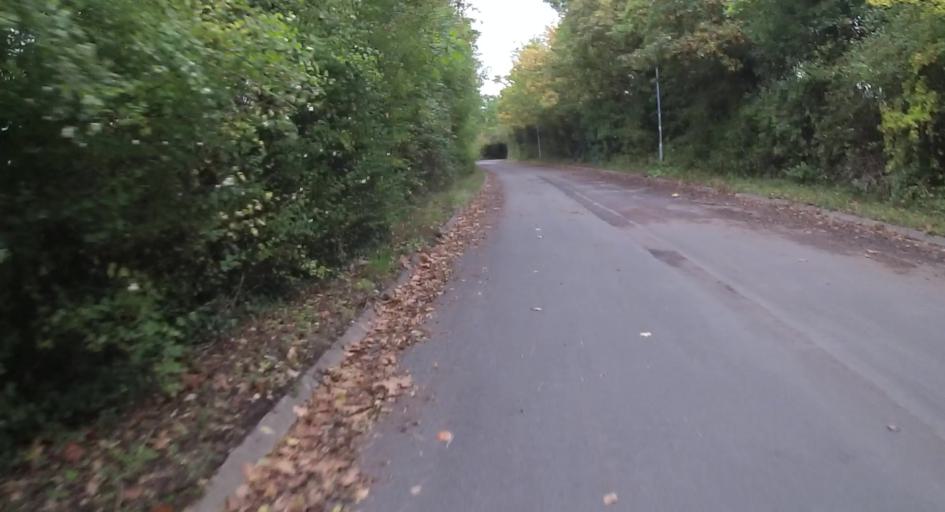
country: GB
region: England
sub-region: Bracknell Forest
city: Binfield
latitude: 51.4138
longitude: -0.7841
